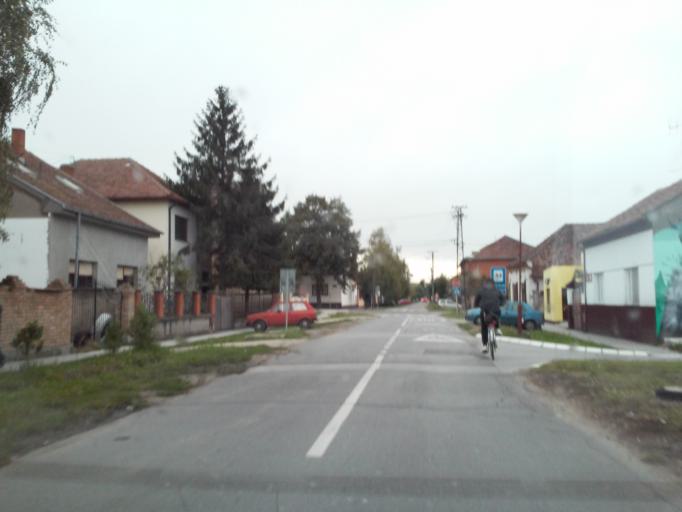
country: RS
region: Autonomna Pokrajina Vojvodina
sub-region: Severnobanatski Okrug
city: Kikinda
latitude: 45.8262
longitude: 20.4616
